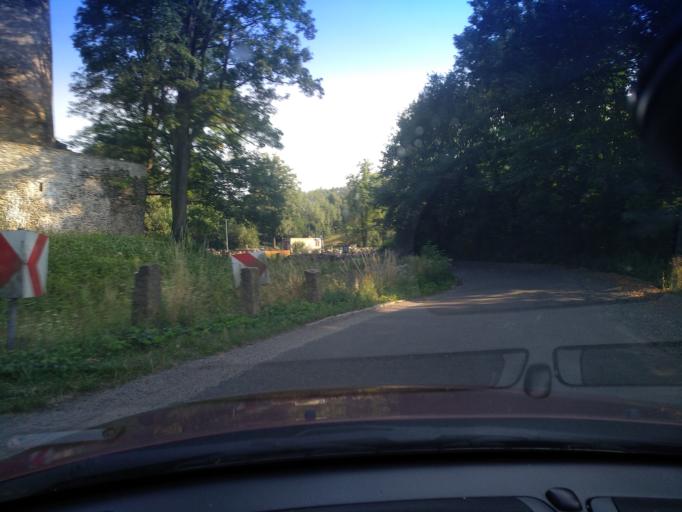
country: PL
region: Lower Silesian Voivodeship
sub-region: Powiat lubanski
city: Lesna
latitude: 50.9975
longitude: 15.2845
